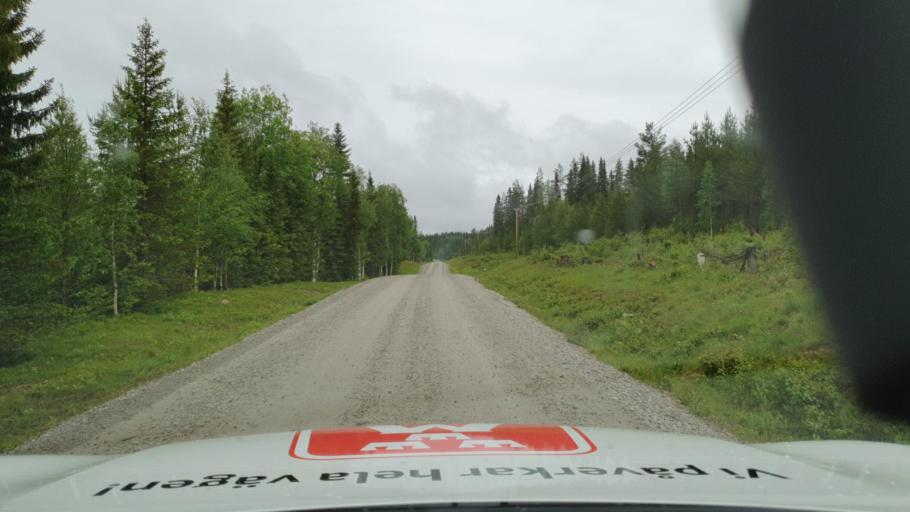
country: SE
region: Vaesterbotten
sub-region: Asele Kommun
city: Asele
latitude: 63.9694
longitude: 16.8809
